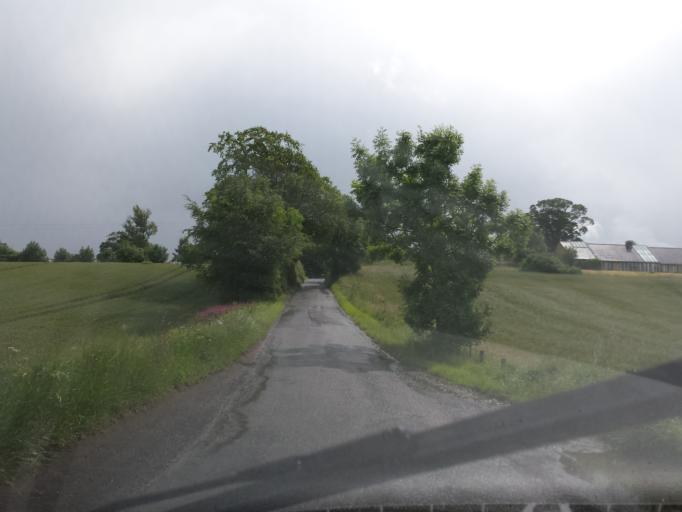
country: GB
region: Scotland
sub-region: The Scottish Borders
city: Saint Boswells
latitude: 55.5960
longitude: -2.6427
